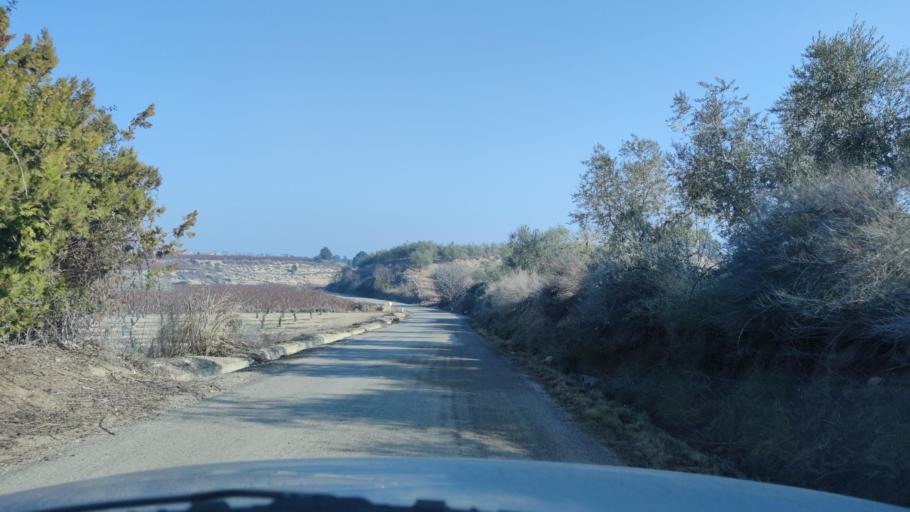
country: ES
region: Catalonia
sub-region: Provincia de Lleida
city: Seros
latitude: 41.4650
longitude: 0.3946
